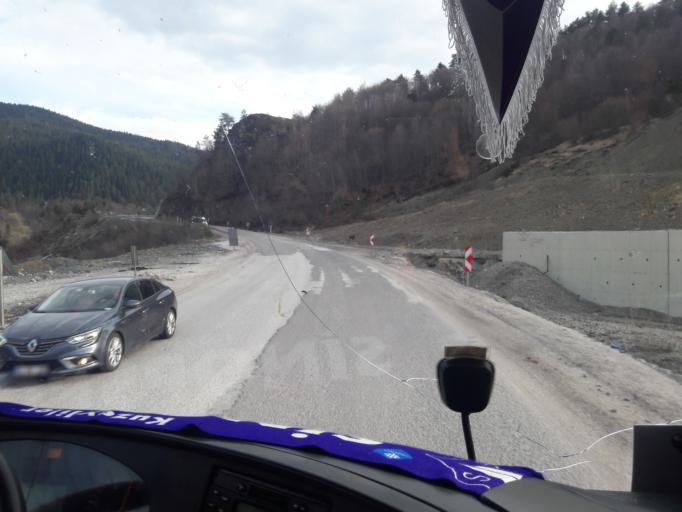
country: TR
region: Kastamonu
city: Kuzyaka
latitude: 41.1106
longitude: 33.7505
